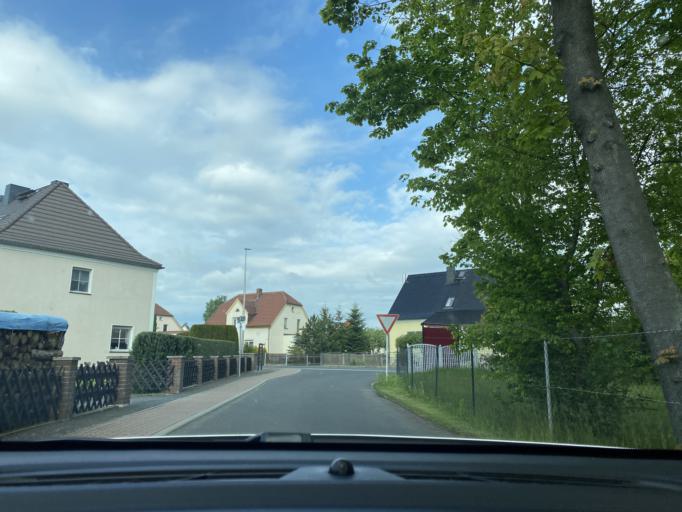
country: DE
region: Saxony
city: Rothenburg
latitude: 51.3280
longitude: 14.9633
